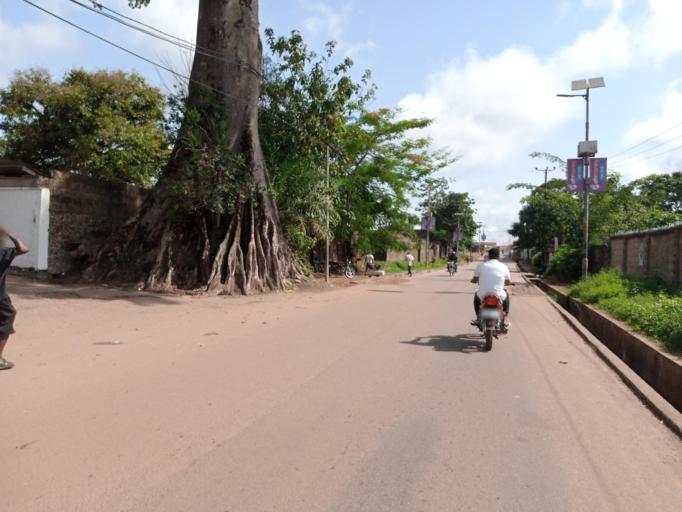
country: SL
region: Southern Province
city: Bo
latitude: 7.9621
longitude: -11.7415
